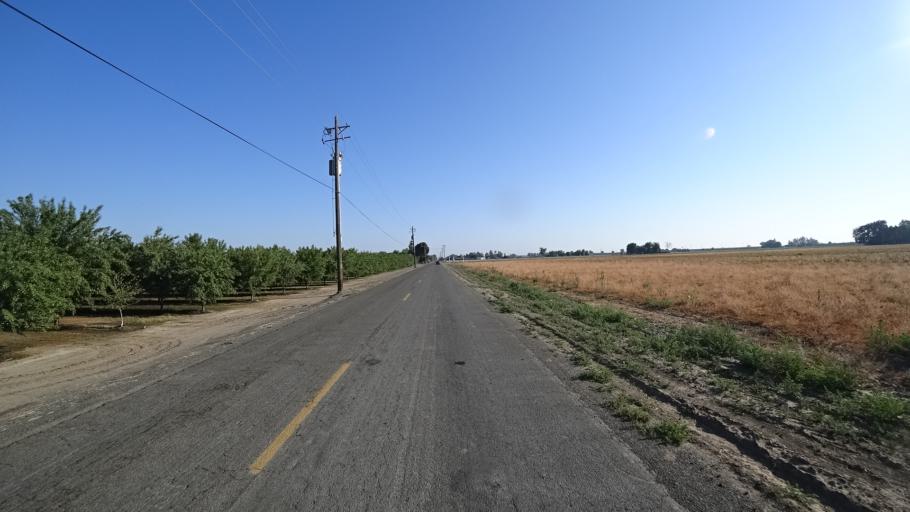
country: US
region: California
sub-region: Kings County
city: Lemoore
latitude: 36.2639
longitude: -119.7446
